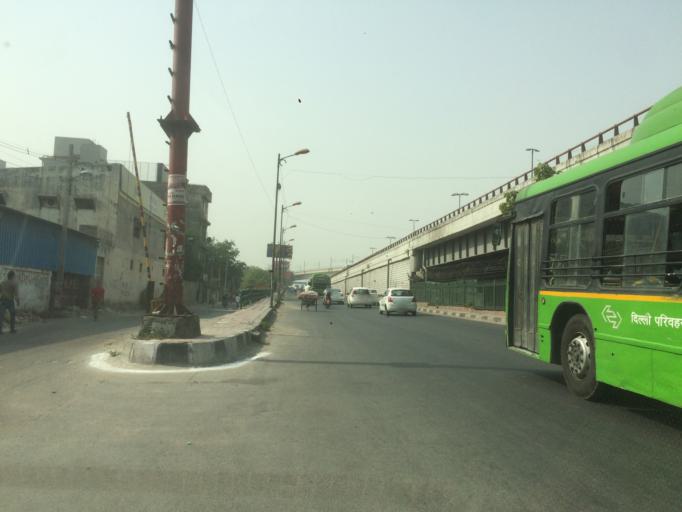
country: IN
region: NCT
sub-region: North West Delhi
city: Pitampura
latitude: 28.6361
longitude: 77.1308
